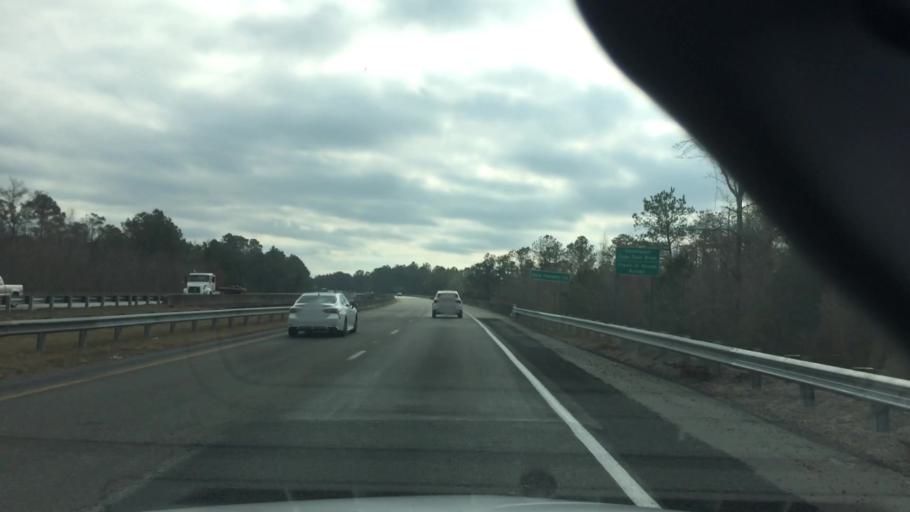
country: US
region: North Carolina
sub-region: New Hanover County
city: Castle Hayne
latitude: 34.3665
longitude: -77.8884
